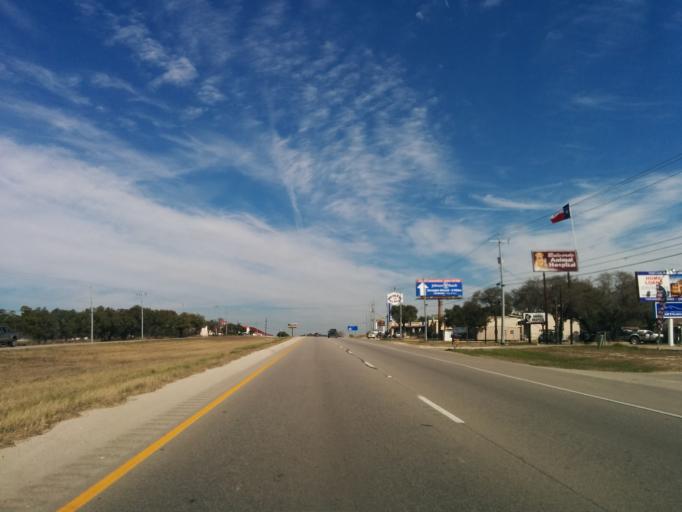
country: US
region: Texas
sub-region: Comal County
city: Bulverde
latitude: 29.7350
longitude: -98.4393
